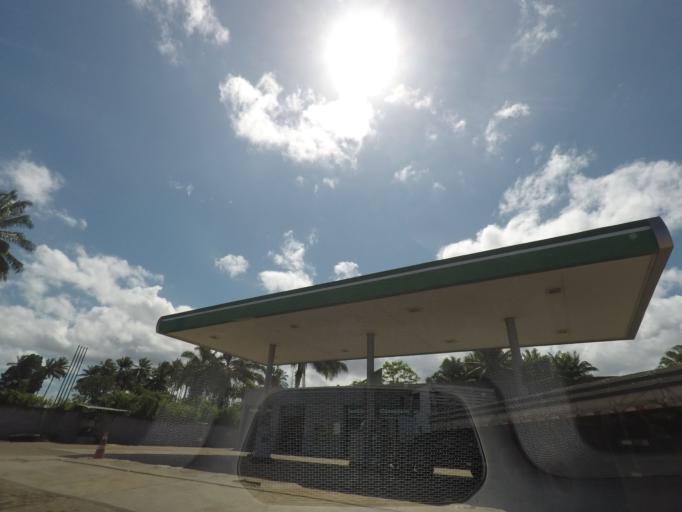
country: BR
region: Bahia
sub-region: Taperoa
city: Taperoa
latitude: -13.5469
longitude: -39.0988
